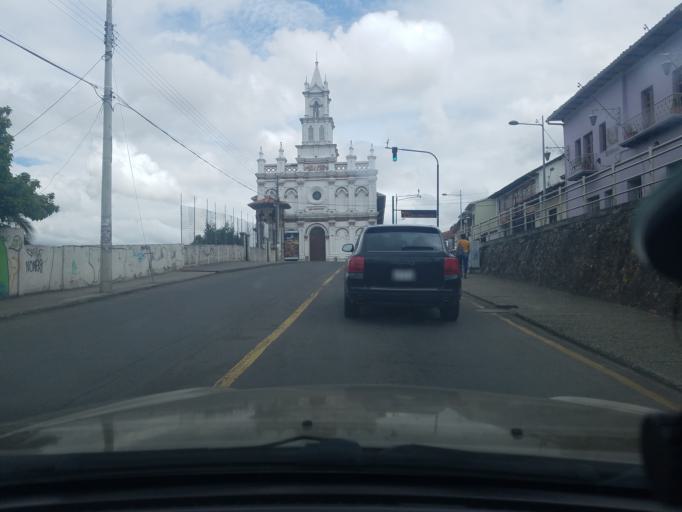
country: EC
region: Azuay
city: Cuenca
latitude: -2.9037
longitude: -79.0013
